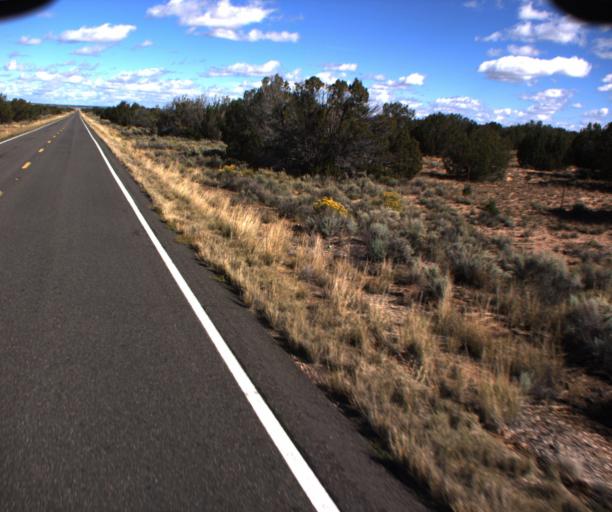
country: US
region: Arizona
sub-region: Apache County
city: Saint Johns
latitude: 34.8722
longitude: -109.2378
